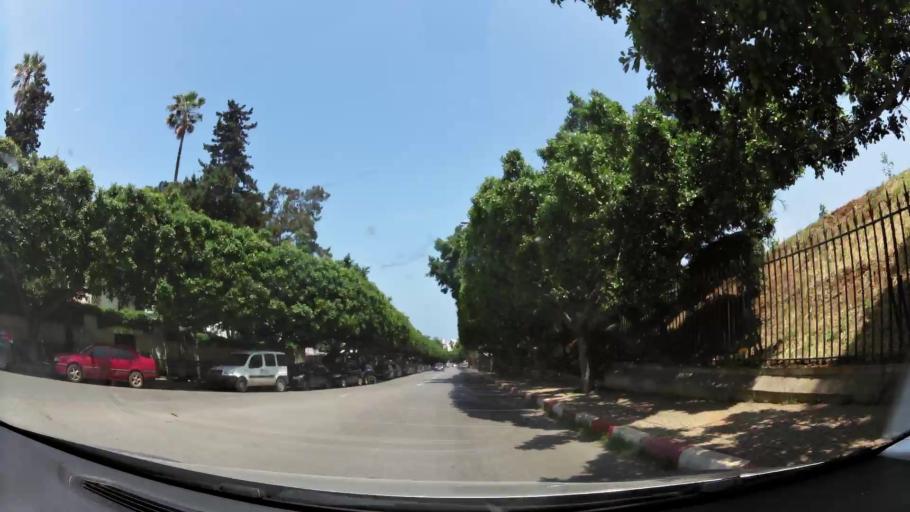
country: MA
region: Rabat-Sale-Zemmour-Zaer
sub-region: Rabat
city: Rabat
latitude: 34.0117
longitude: -6.8259
